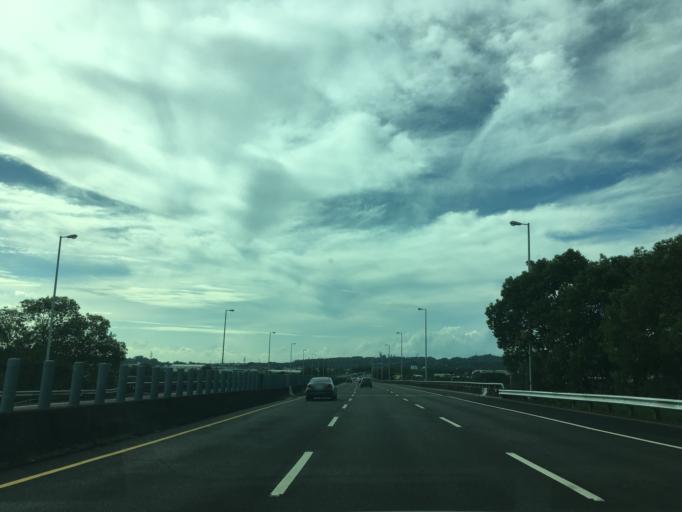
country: TW
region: Taiwan
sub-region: Chiayi
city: Jiayi Shi
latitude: 23.5037
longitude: 120.4912
